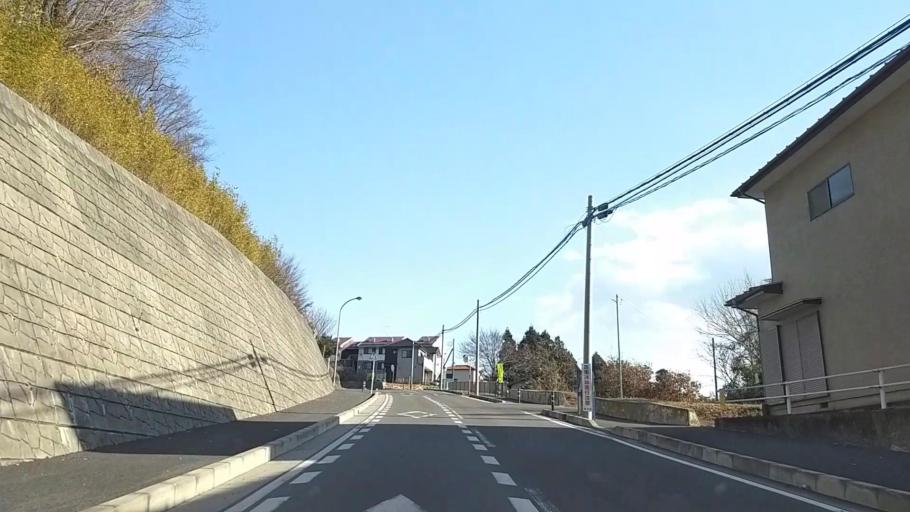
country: JP
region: Kanagawa
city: Atsugi
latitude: 35.4567
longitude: 139.3244
